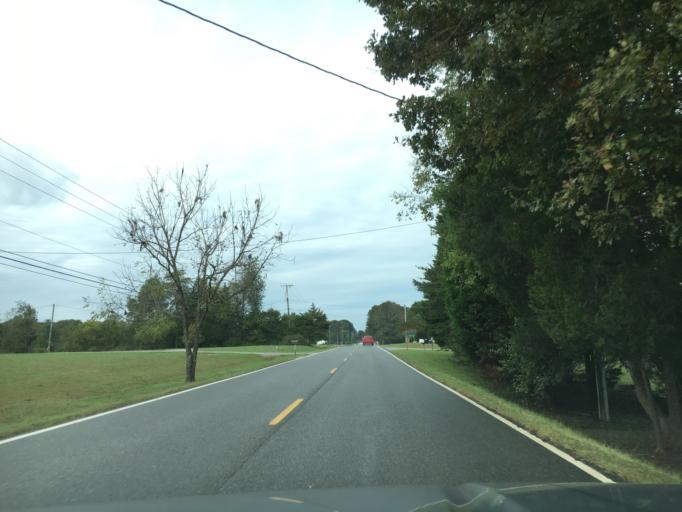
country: US
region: Virginia
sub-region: Goochland County
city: Goochland
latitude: 37.7255
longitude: -77.8313
